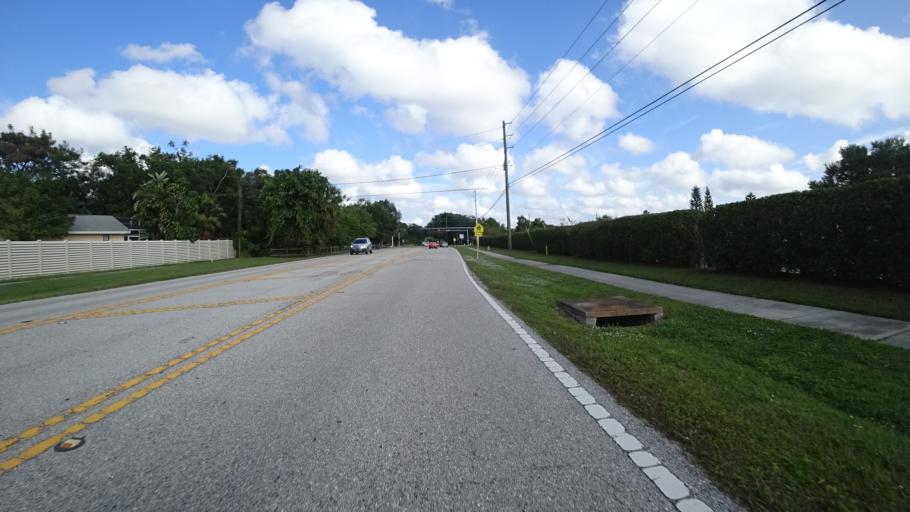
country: US
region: Florida
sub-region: Sarasota County
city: North Sarasota
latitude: 27.4022
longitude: -82.5135
